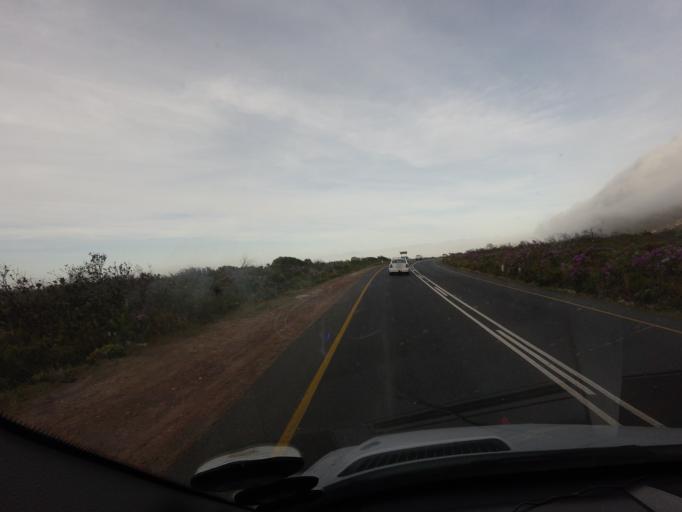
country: ZA
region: Western Cape
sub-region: City of Cape Town
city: Bergvliet
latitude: -34.0872
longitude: 18.4218
